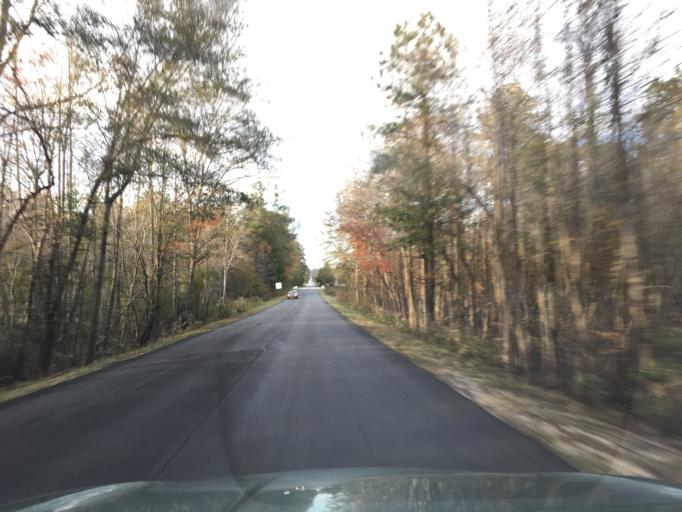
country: US
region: South Carolina
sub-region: Lexington County
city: Red Bank
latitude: 33.7204
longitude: -81.3565
